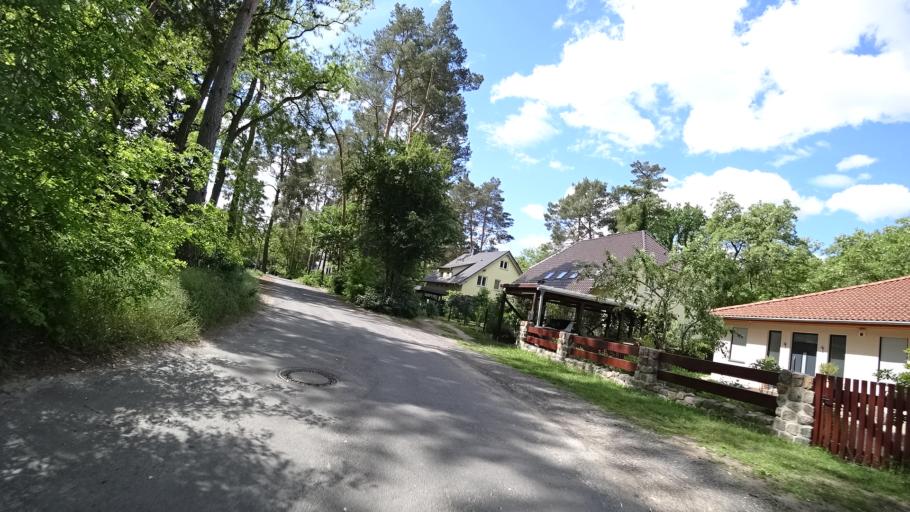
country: DE
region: Berlin
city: Lichtenrade
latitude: 52.3609
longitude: 13.3987
